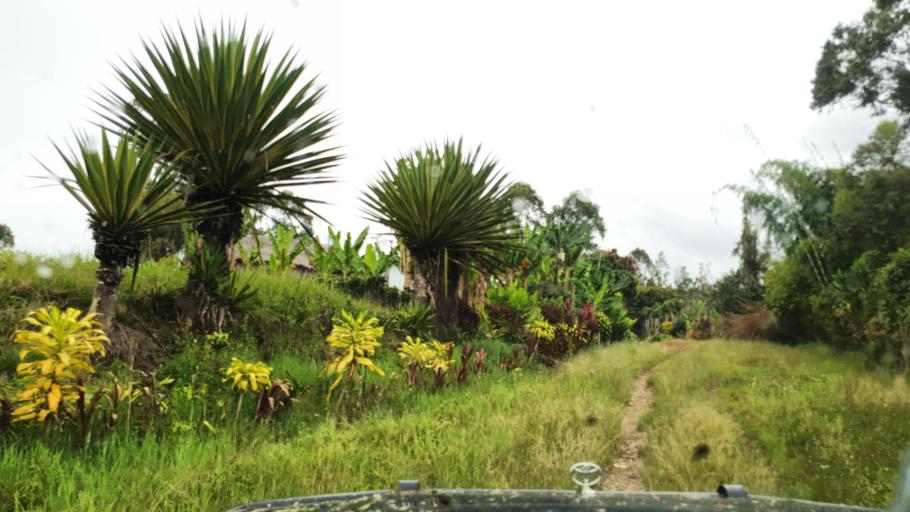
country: PG
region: Jiwaka
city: Minj
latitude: -5.9454
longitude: 144.7678
